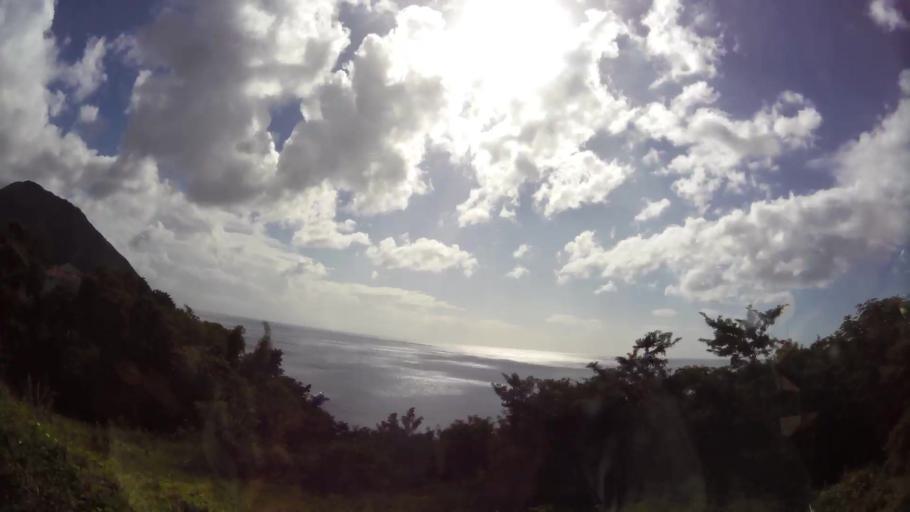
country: DM
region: Saint George
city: Roseau
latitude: 15.2898
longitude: -61.3761
